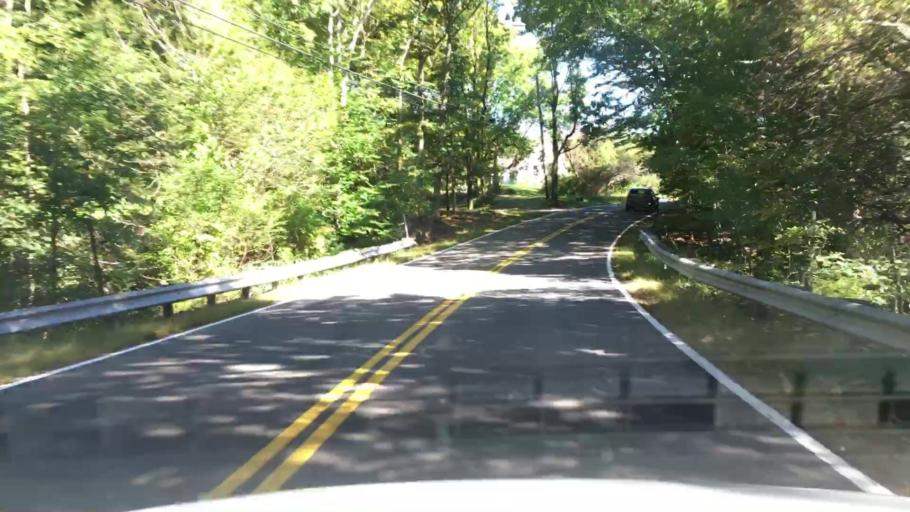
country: US
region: Maine
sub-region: York County
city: York Harbor
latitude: 43.1102
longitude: -70.6720
